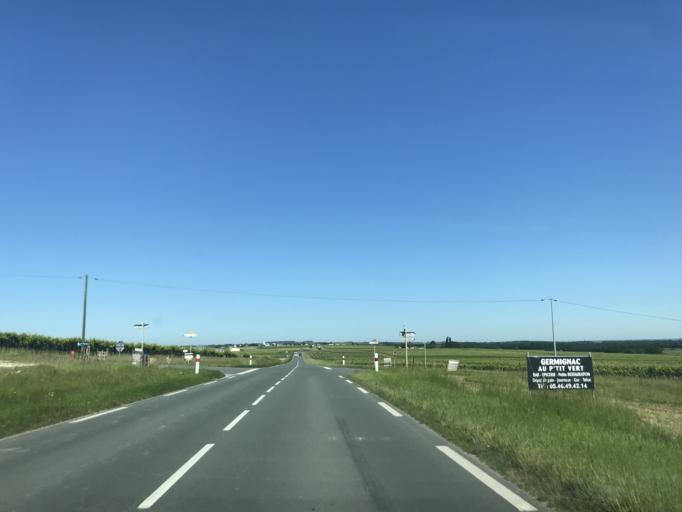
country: FR
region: Poitou-Charentes
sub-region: Departement de la Charente
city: Chateaubernard
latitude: 45.5450
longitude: -0.3509
